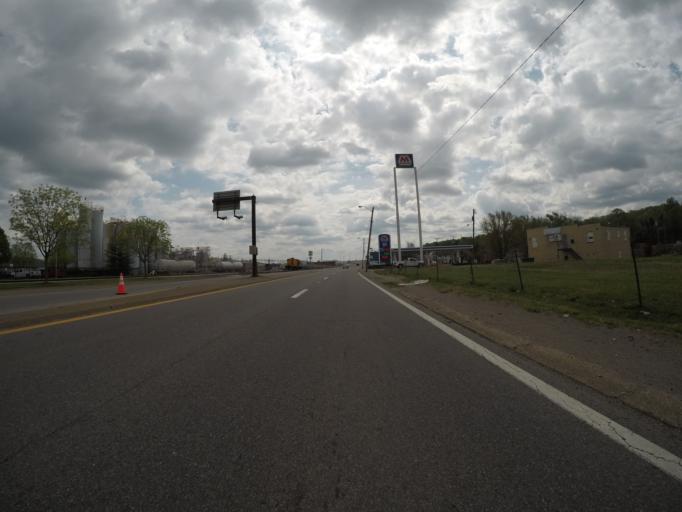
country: US
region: West Virginia
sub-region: Kanawha County
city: South Charleston
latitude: 38.3673
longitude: -81.6851
